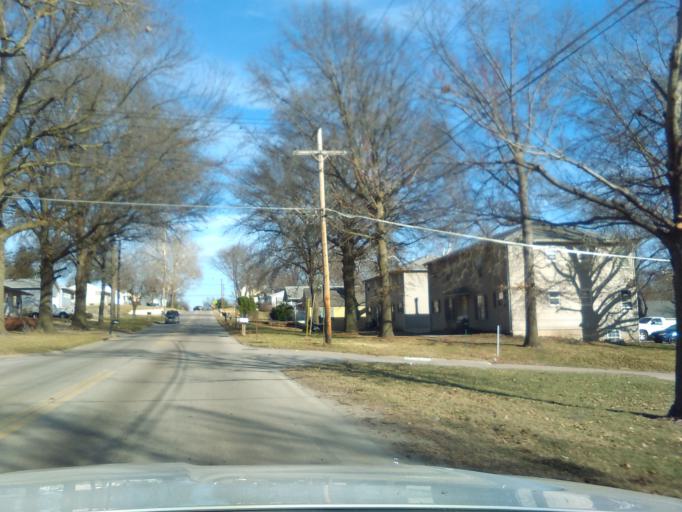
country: US
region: Nebraska
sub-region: Otoe County
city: Nebraska City
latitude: 40.6731
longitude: -95.8682
